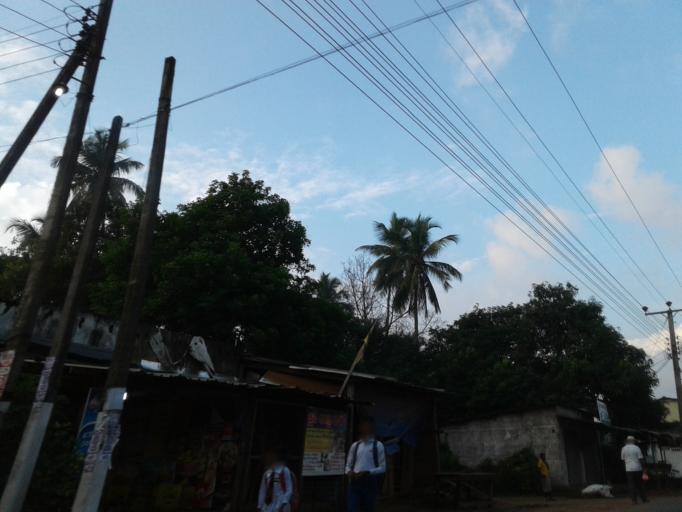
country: LK
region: Western
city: Mulleriyawa
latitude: 6.9682
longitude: 80.0000
